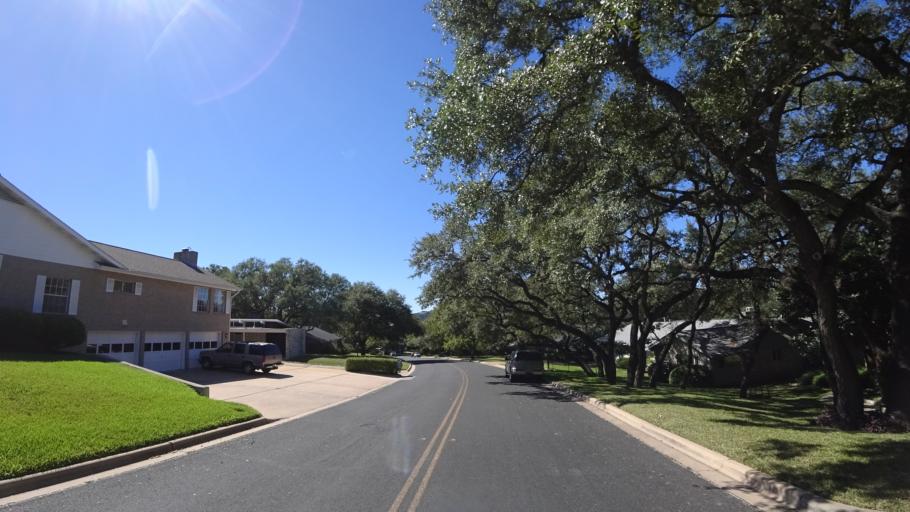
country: US
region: Texas
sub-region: Travis County
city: West Lake Hills
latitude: 30.3088
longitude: -97.7693
